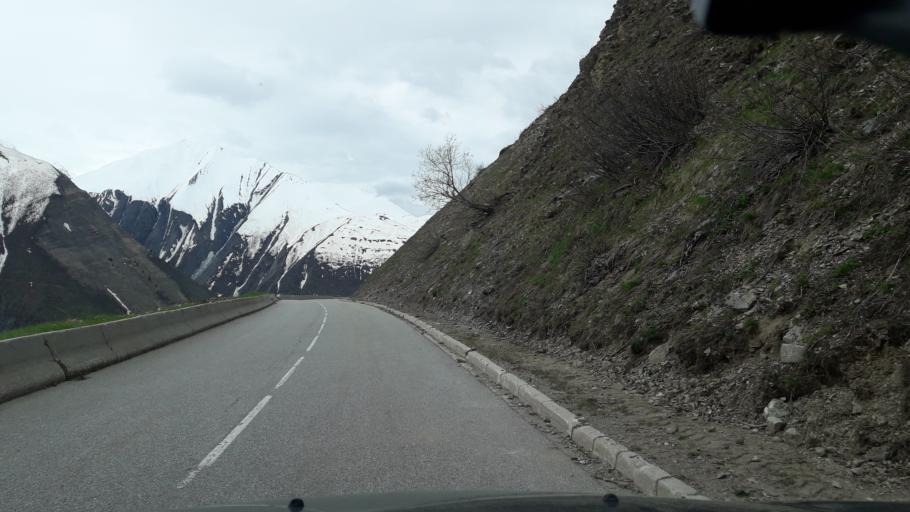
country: FR
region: Rhone-Alpes
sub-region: Departement de l'Isere
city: Huez
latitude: 45.2208
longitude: 6.1360
